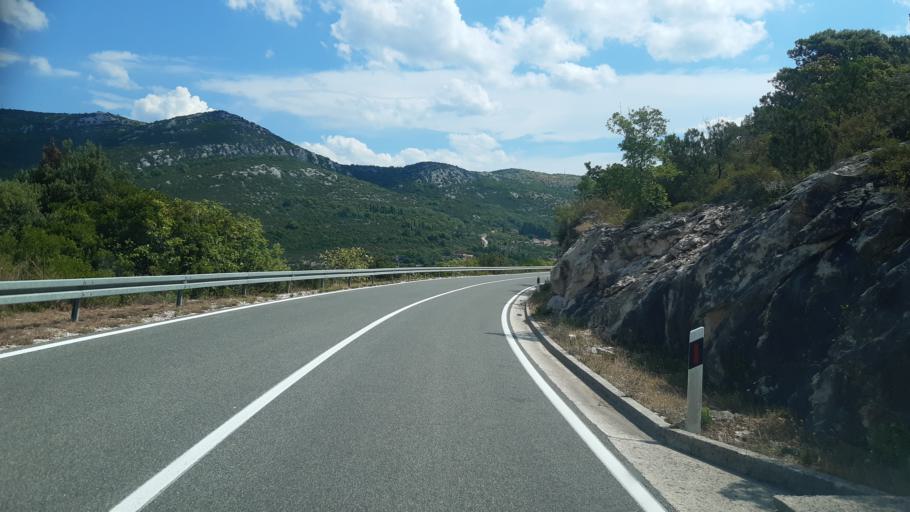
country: HR
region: Dubrovacko-Neretvanska
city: Ston
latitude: 42.8321
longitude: 17.7375
